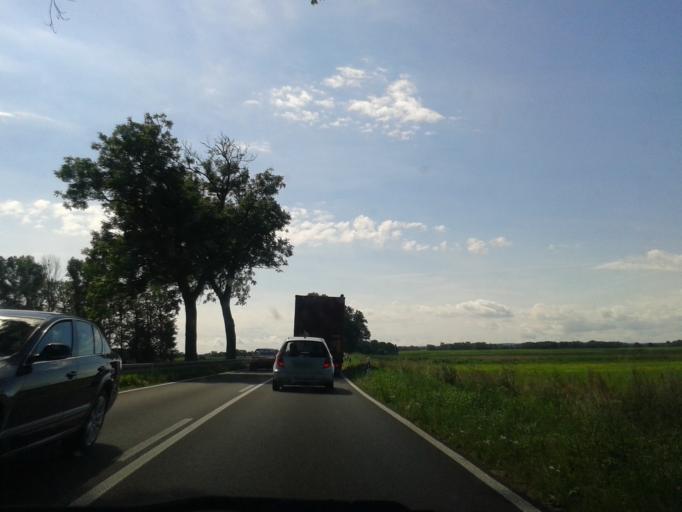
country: DE
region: Mecklenburg-Vorpommern
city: Ferdinandshof
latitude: 53.6855
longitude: 13.8819
